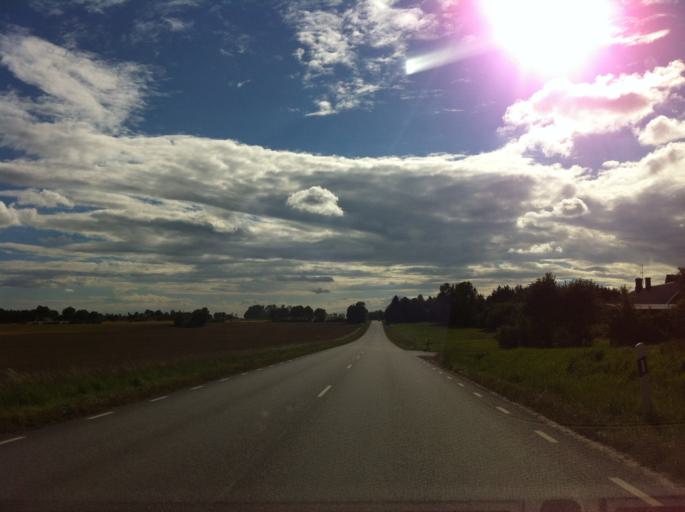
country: SE
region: Skane
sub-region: Hoors Kommun
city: Hoeoer
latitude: 56.0114
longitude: 13.5403
